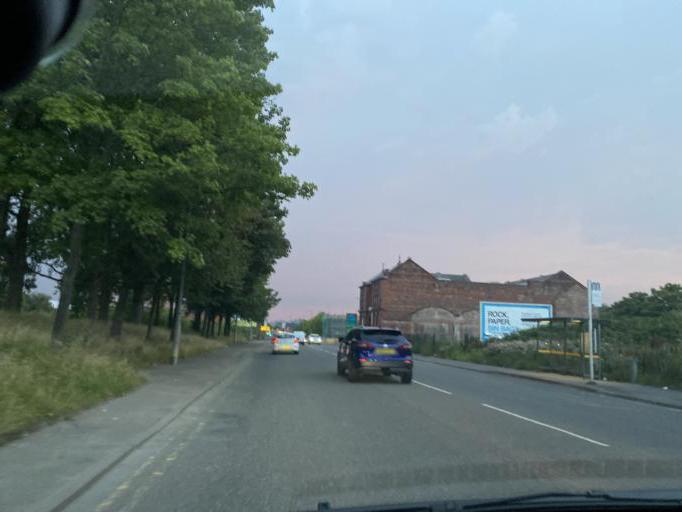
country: GB
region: England
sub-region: Manchester
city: Longsight
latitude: 53.4736
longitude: -2.1854
